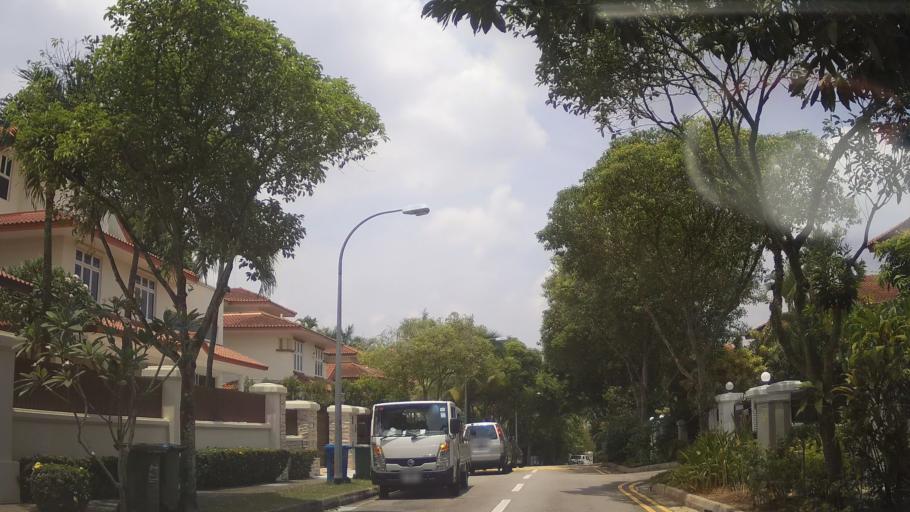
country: MY
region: Johor
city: Johor Bahru
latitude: 1.3717
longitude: 103.7727
